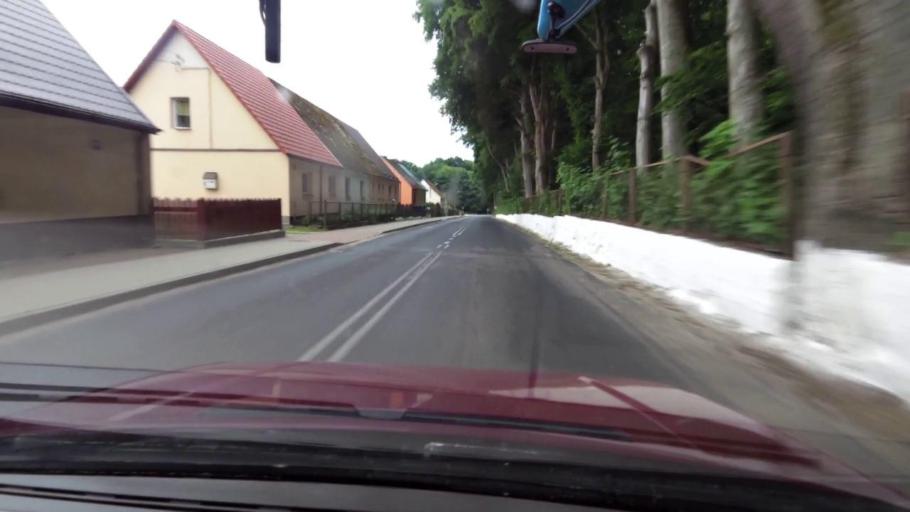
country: PL
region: West Pomeranian Voivodeship
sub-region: Powiat koszalinski
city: Polanow
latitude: 54.1398
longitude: 16.5229
